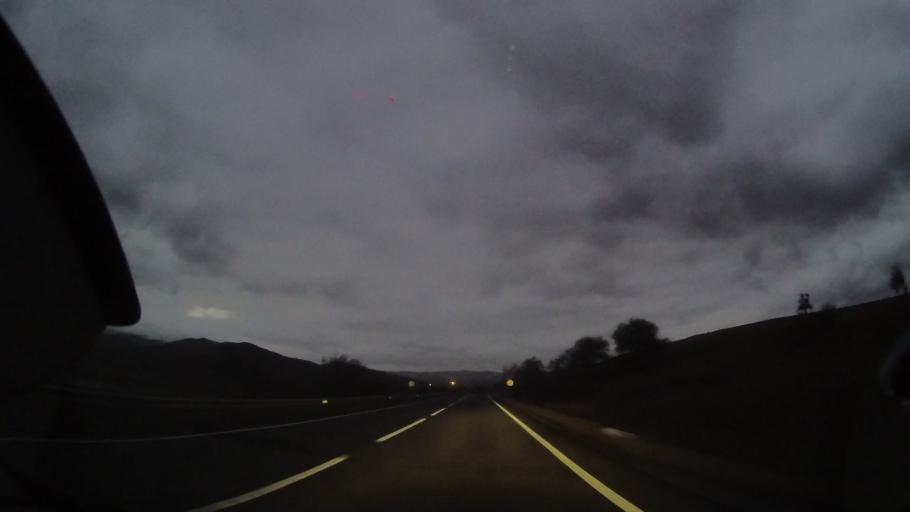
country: RO
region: Cluj
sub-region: Comuna Sancraiu
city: Sancraiu
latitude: 46.8756
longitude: 22.9539
